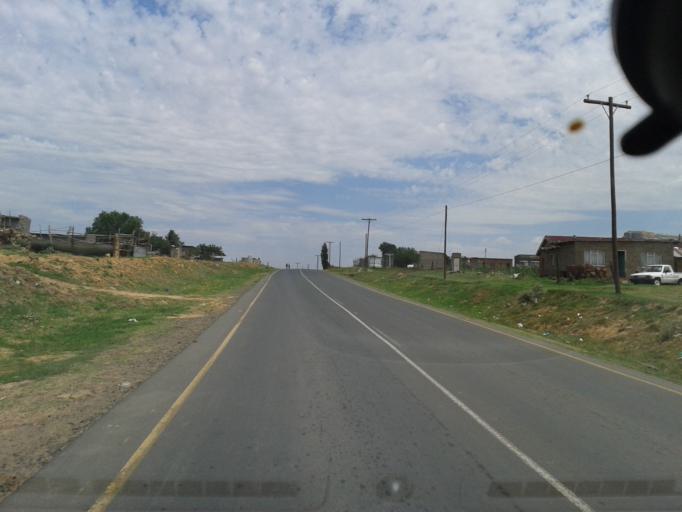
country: LS
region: Maseru
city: Maseru
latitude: -29.3559
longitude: 27.5891
